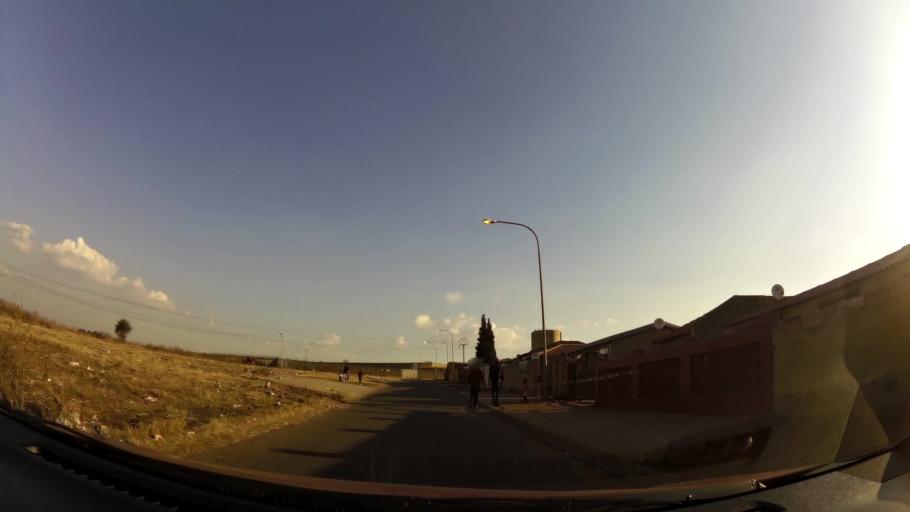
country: ZA
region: Gauteng
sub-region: City of Johannesburg Metropolitan Municipality
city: Soweto
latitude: -26.2302
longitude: 27.8574
